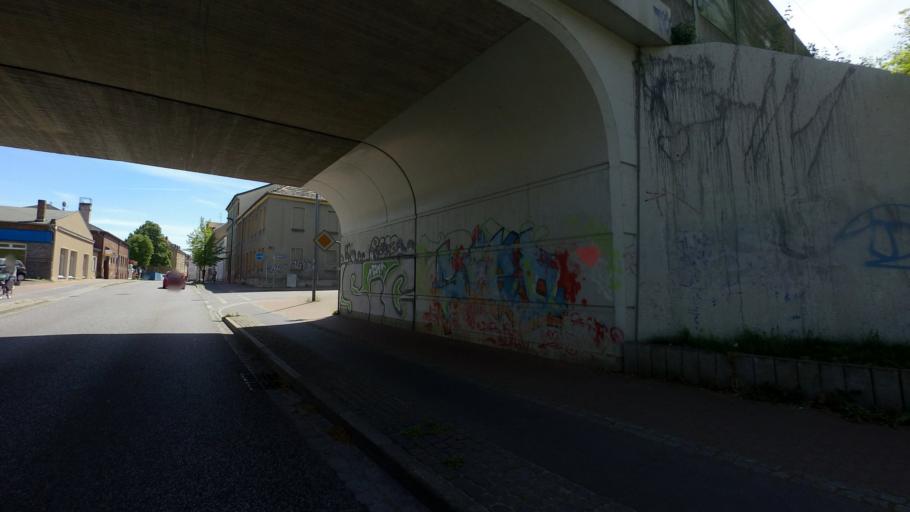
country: DE
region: Brandenburg
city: Luckenwalde
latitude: 52.0952
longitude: 13.1655
